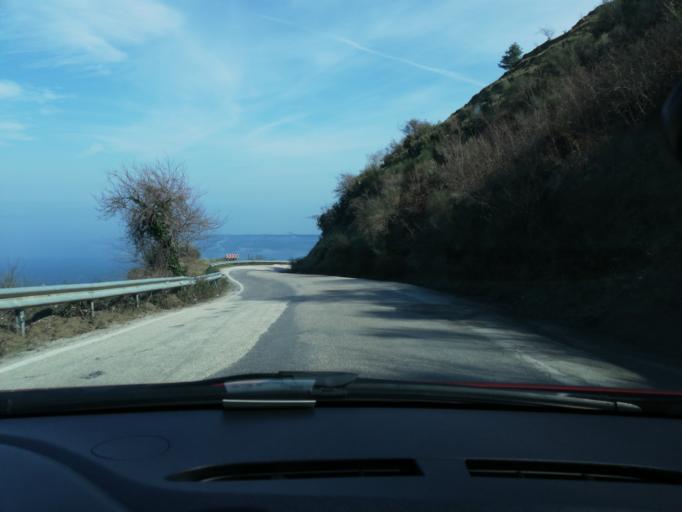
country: TR
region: Bartin
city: Kurucasile
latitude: 41.8270
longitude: 32.6511
